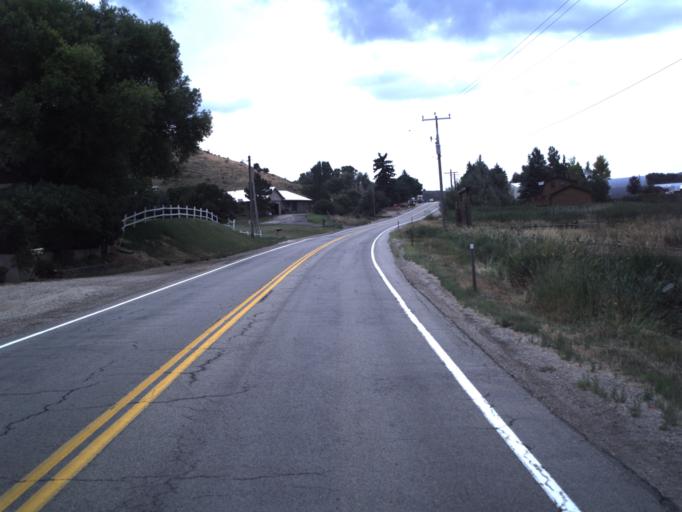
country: US
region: Utah
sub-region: Summit County
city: Oakley
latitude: 40.7302
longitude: -111.3454
